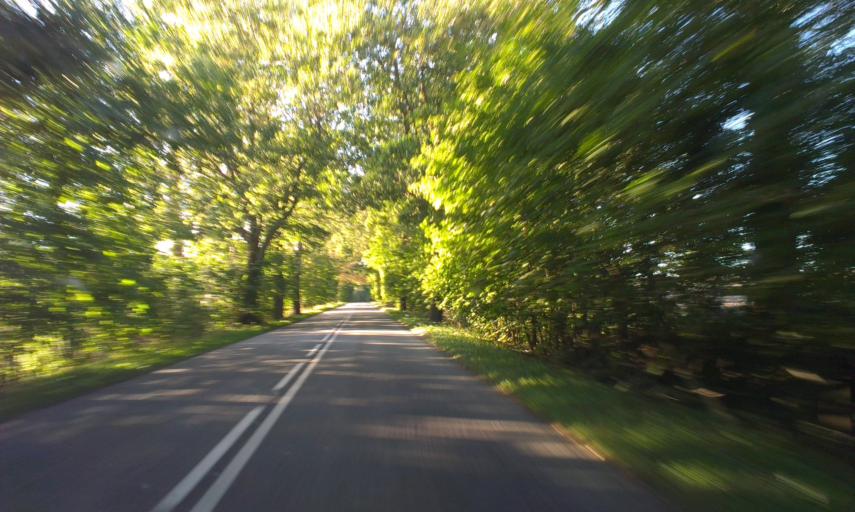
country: PL
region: Pomeranian Voivodeship
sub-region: Powiat czluchowski
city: Debrzno
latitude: 53.6313
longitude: 17.1688
